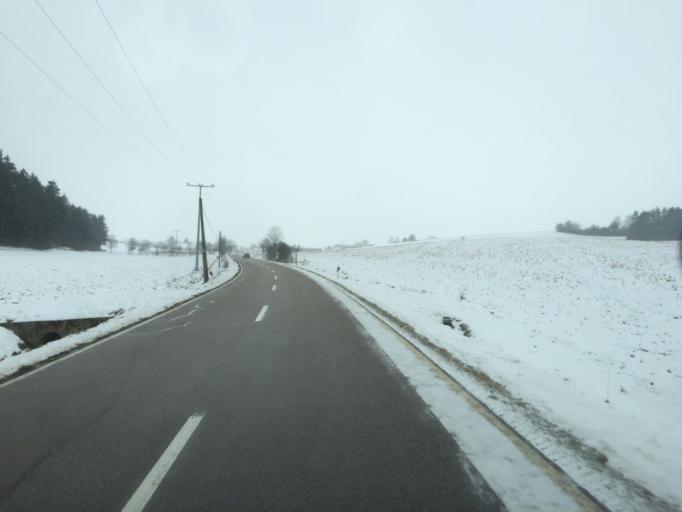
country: DE
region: Bavaria
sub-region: Upper Palatinate
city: Breitenbrunn
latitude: 49.3395
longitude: 11.9940
